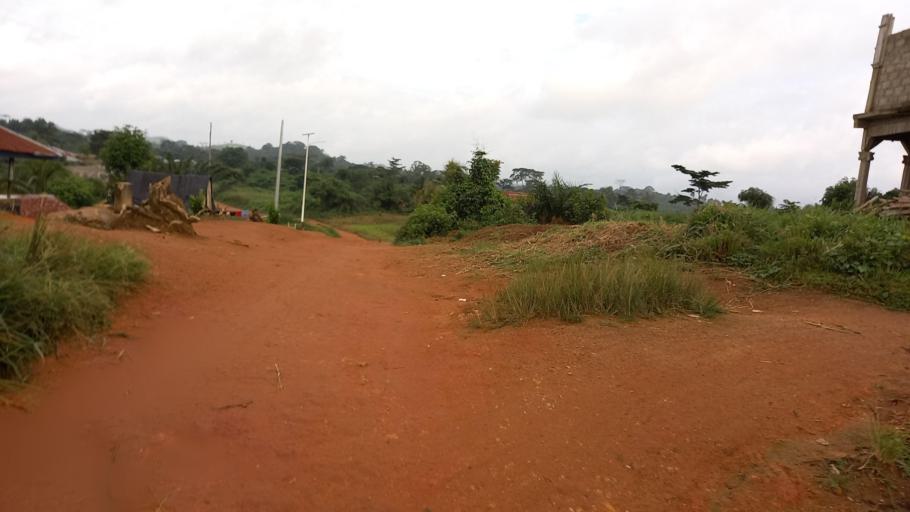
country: SL
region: Eastern Province
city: Kailahun
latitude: 8.2760
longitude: -10.5838
